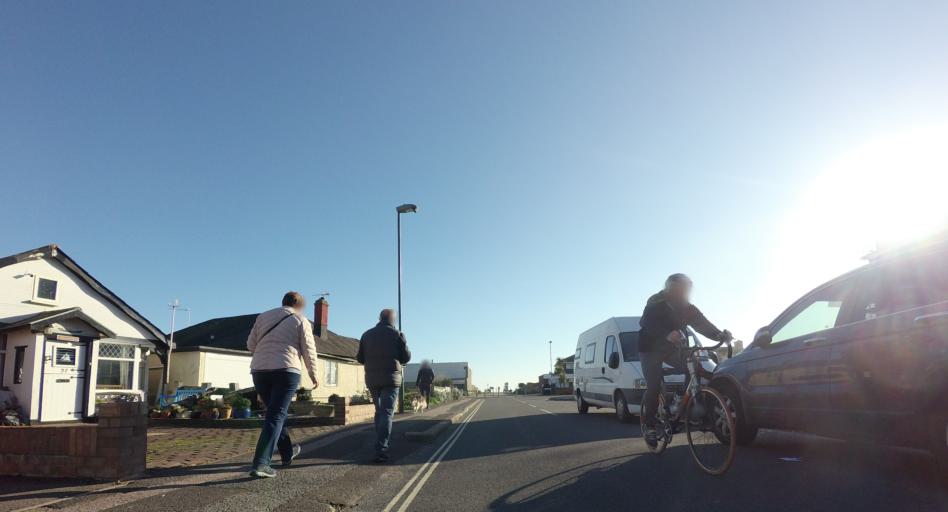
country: GB
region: England
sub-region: West Sussex
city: Shoreham-by-Sea
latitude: 50.8285
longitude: -0.2719
